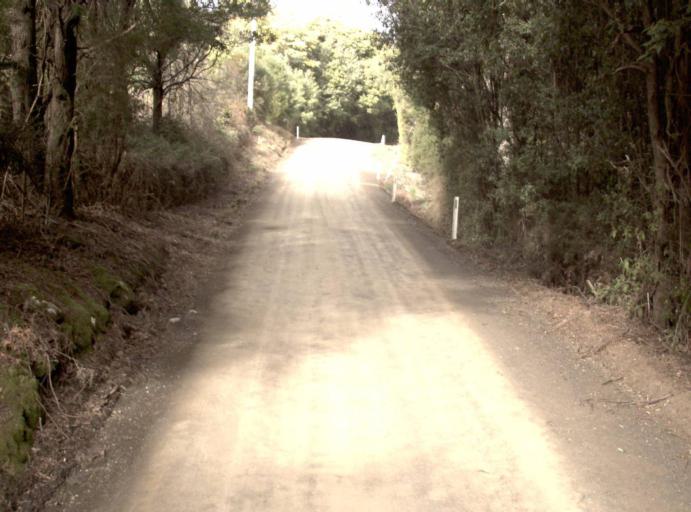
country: AU
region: Tasmania
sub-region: Launceston
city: Mayfield
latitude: -41.2766
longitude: 147.1886
